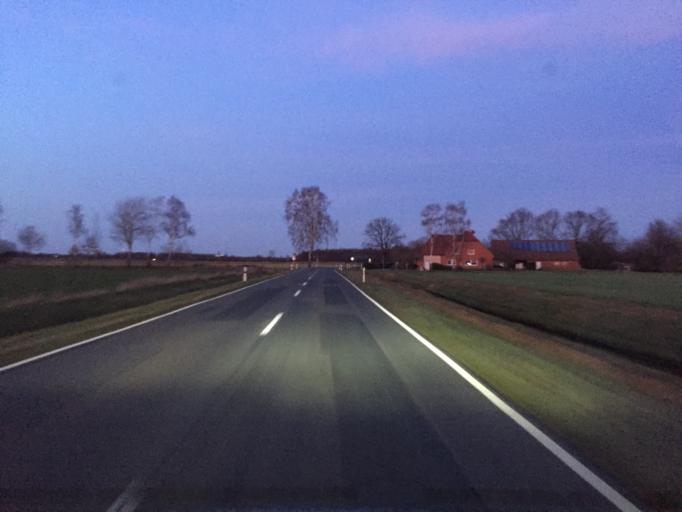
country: DE
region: Lower Saxony
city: Kirchdorf
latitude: 52.6293
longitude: 8.8860
